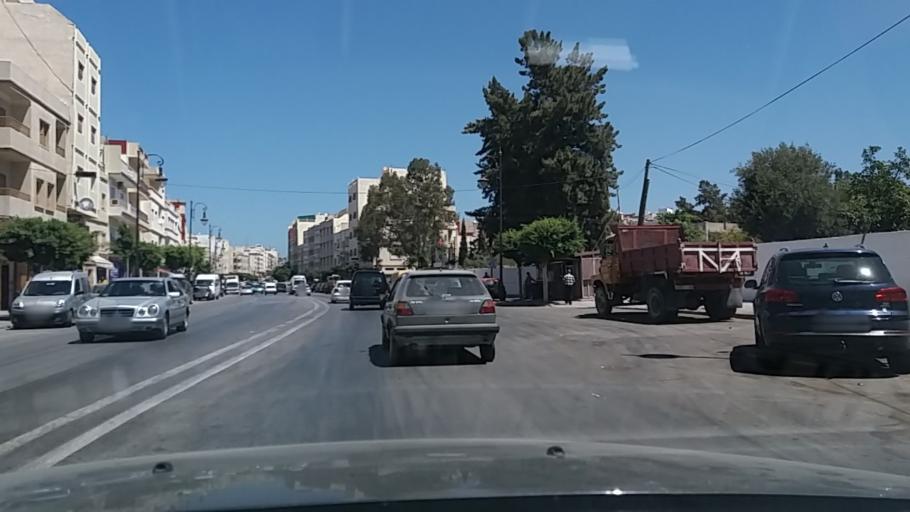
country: MA
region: Tanger-Tetouan
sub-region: Tanger-Assilah
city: Tangier
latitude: 35.7583
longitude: -5.7963
